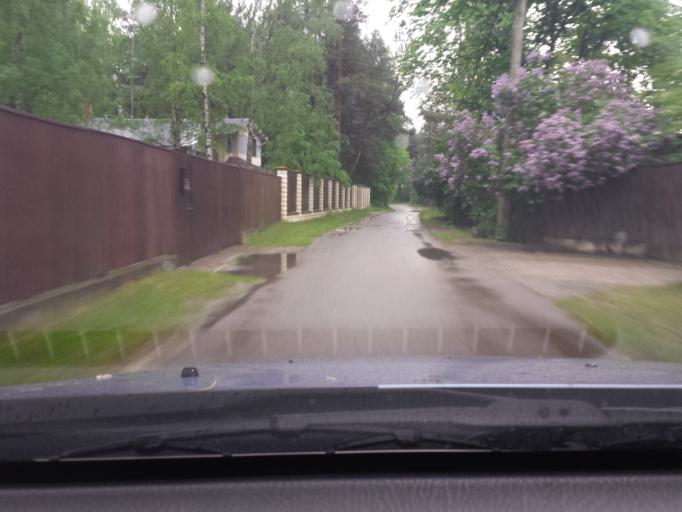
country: LV
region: Riga
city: Bolderaja
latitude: 57.0525
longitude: 24.1021
